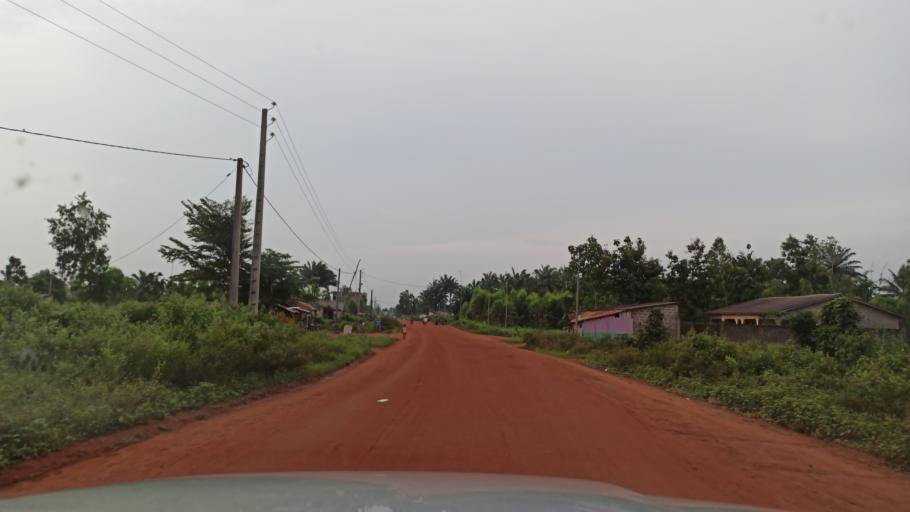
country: BJ
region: Queme
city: Porto-Novo
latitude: 6.5150
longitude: 2.6834
